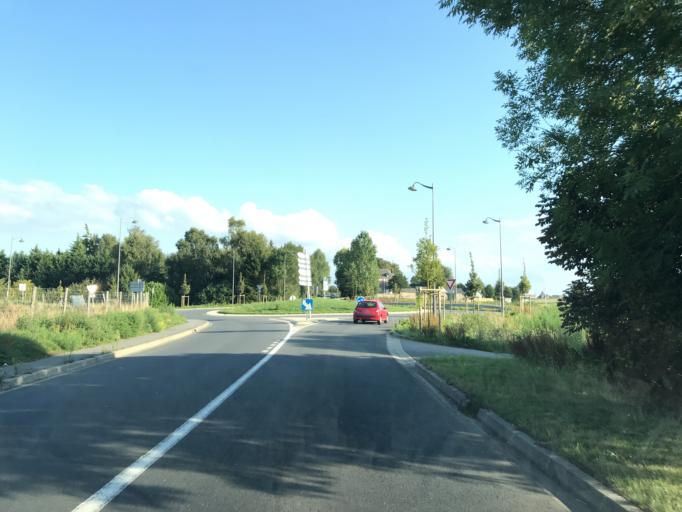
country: FR
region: Haute-Normandie
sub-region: Departement de la Seine-Maritime
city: Beuzeville-la-Grenier
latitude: 49.6020
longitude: 0.4166
